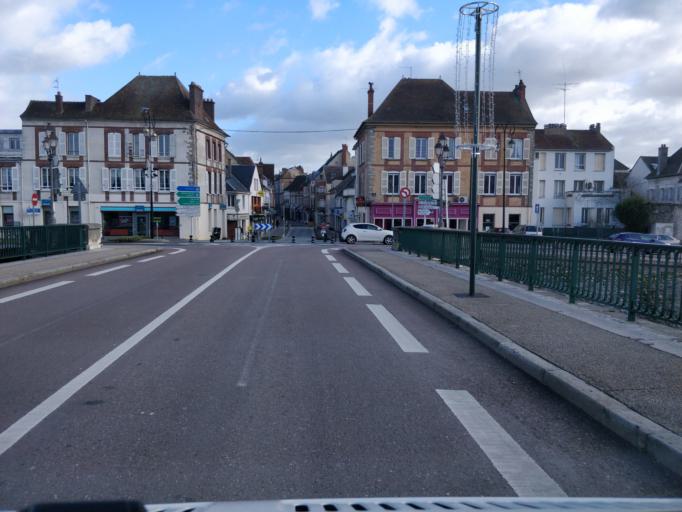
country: FR
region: Bourgogne
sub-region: Departement de l'Yonne
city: Sens
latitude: 48.1974
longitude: 3.2763
